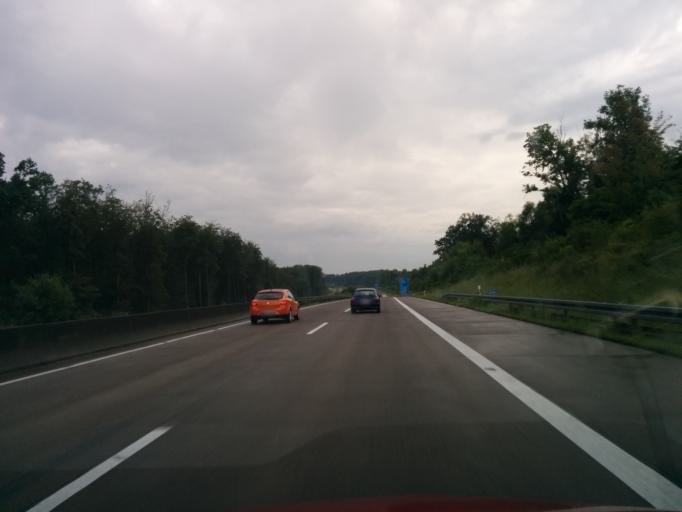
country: DE
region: Hesse
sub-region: Regierungsbezirk Giessen
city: Reiskirchen
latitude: 50.6122
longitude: 8.8482
